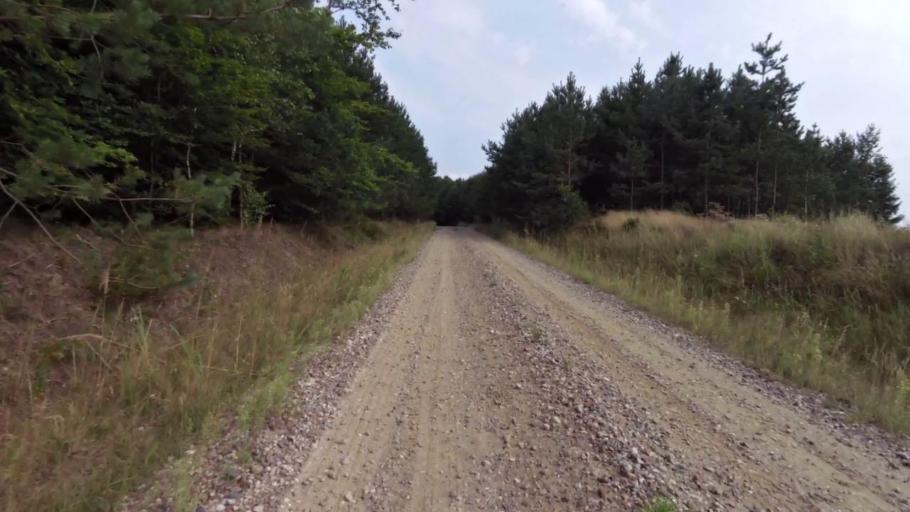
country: PL
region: West Pomeranian Voivodeship
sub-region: Powiat drawski
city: Zlocieniec
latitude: 53.5627
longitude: 15.9205
